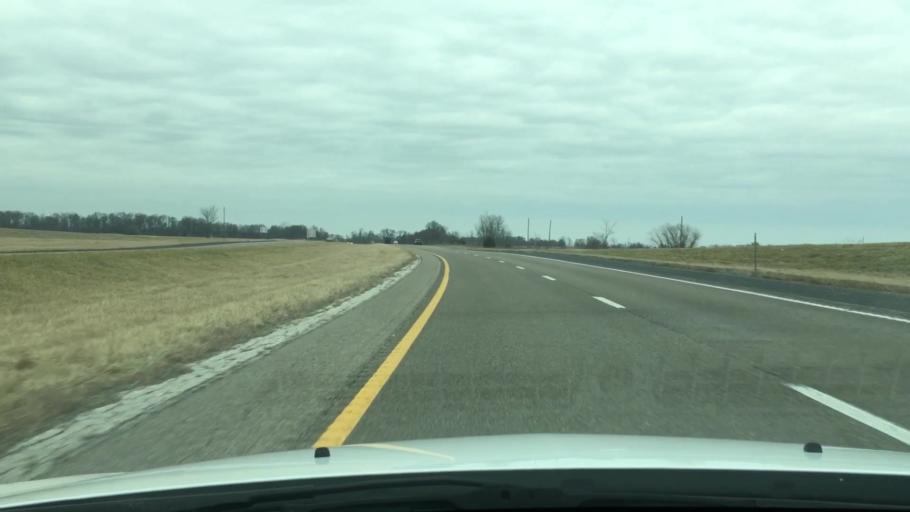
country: US
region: Missouri
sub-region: Audrain County
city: Mexico
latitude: 39.0191
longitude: -91.8859
